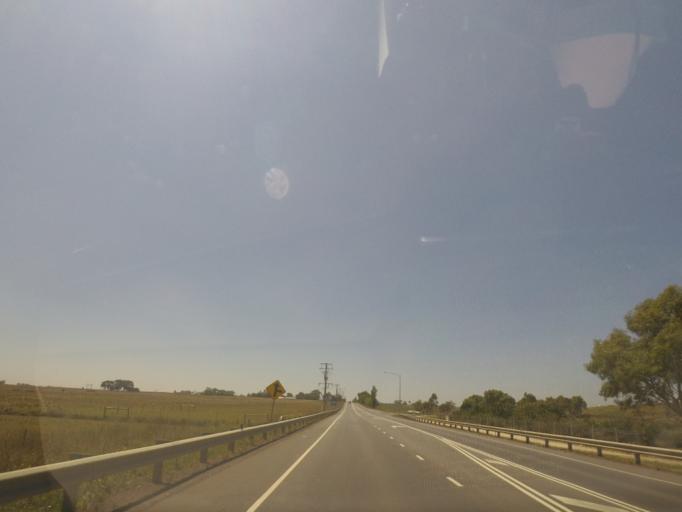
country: AU
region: Victoria
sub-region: Hume
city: Craigieburn
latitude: -37.6028
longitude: 144.9743
